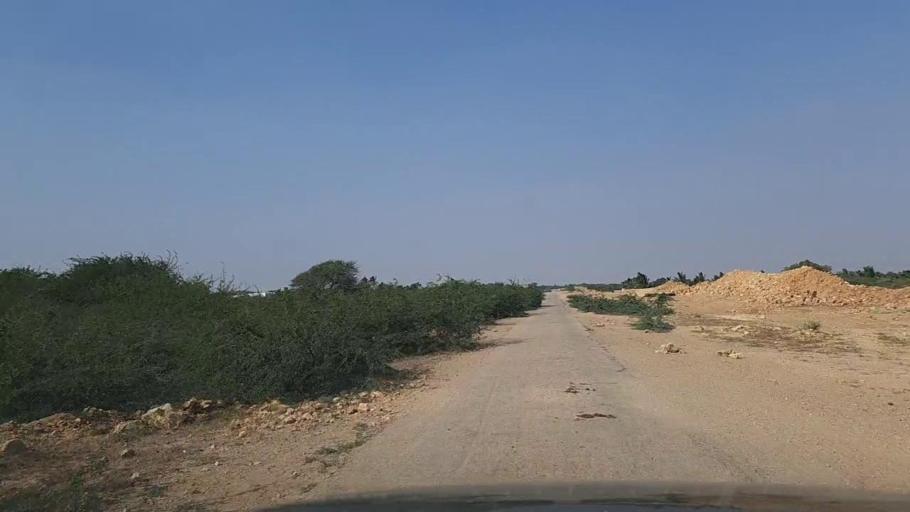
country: PK
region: Sindh
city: Gharo
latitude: 24.7566
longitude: 67.5798
